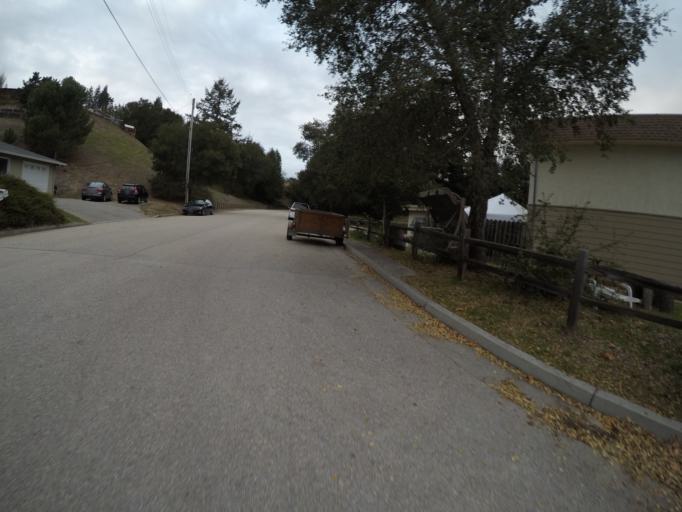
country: US
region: California
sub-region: Santa Cruz County
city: Scotts Valley
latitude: 37.0608
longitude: -122.0104
